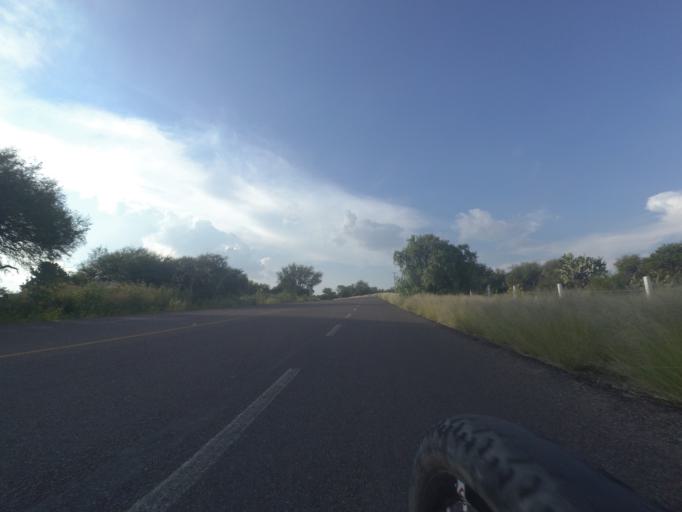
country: MX
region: Aguascalientes
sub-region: Aguascalientes
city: Penuelas (El Cienegal)
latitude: 21.7629
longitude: -102.3516
